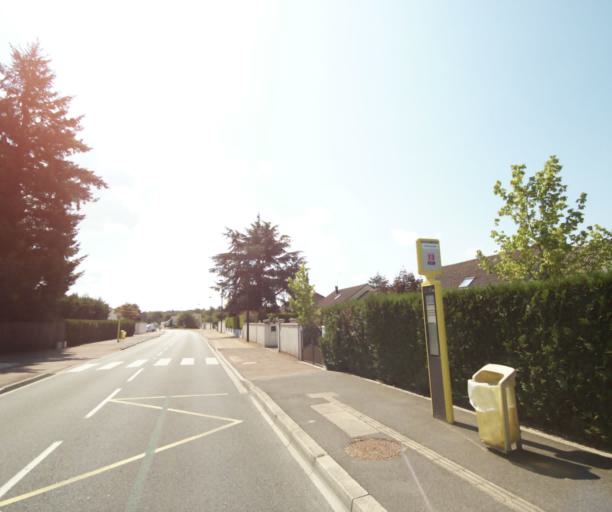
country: FR
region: Centre
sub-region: Departement du Loiret
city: Saint-Cyr-en-Val
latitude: 47.8258
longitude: 1.9754
